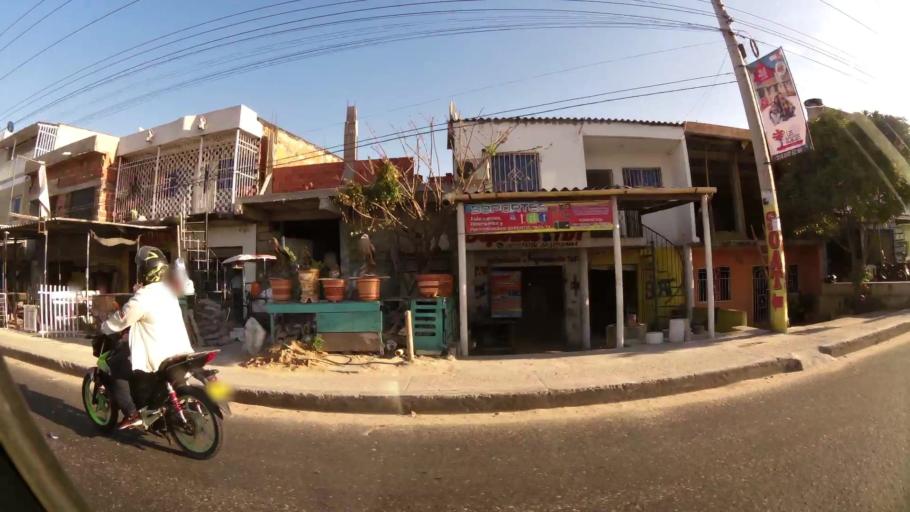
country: CO
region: Atlantico
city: Soledad
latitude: 10.9250
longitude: -74.7906
